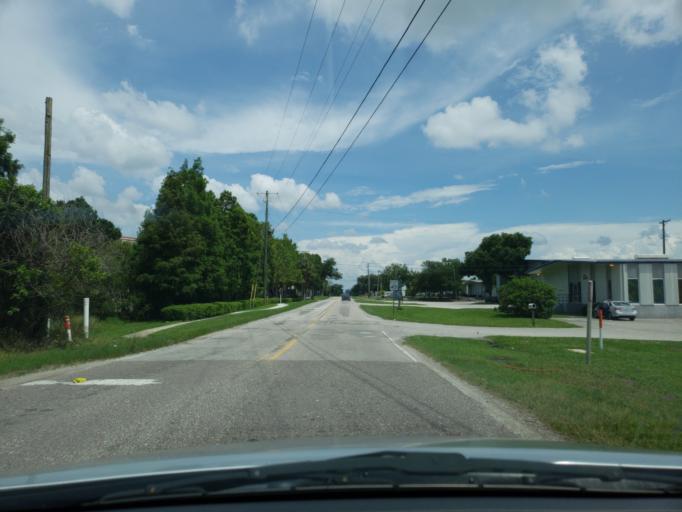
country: US
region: Florida
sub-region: Hillsborough County
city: East Lake-Orient Park
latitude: 27.9660
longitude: -82.3651
